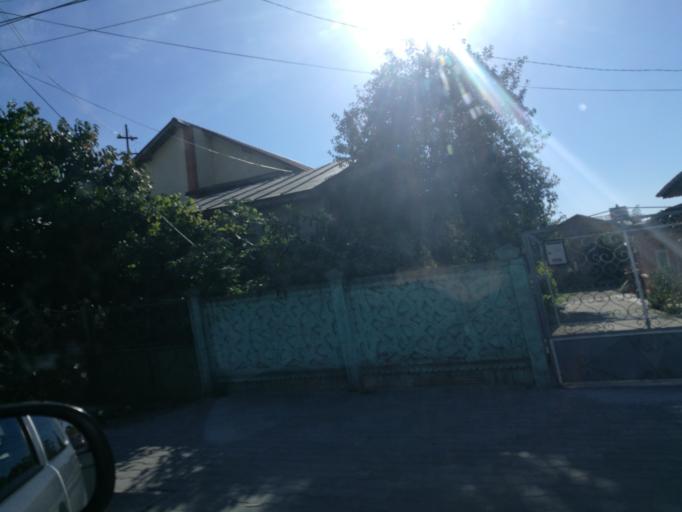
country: RO
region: Ilfov
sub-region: Comuna Dragomiresti-Vale
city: Dragomiresti-Deal
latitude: 44.4582
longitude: 25.9482
